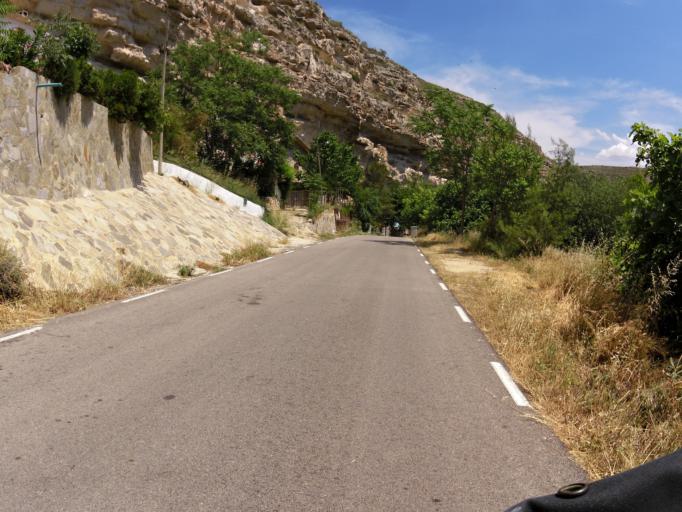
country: ES
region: Castille-La Mancha
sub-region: Provincia de Albacete
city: Jorquera
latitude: 39.1685
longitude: -1.5539
